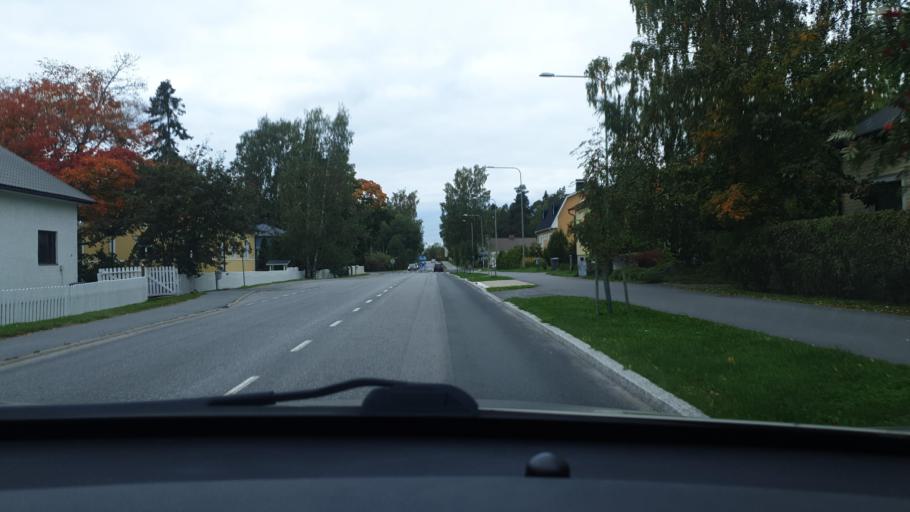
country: FI
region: Ostrobothnia
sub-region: Vaasa
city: Korsholm
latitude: 63.0945
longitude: 21.6692
